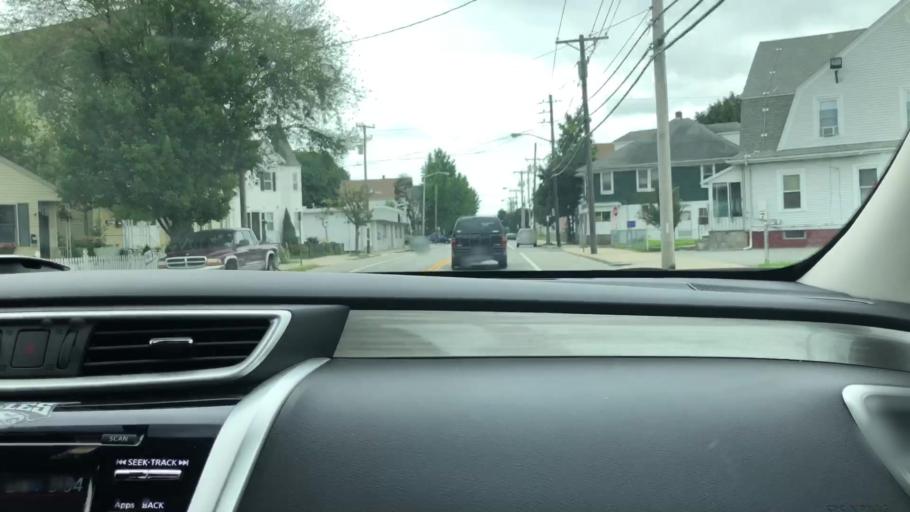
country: US
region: Rhode Island
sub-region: Providence County
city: Central Falls
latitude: 41.8741
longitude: -71.4144
